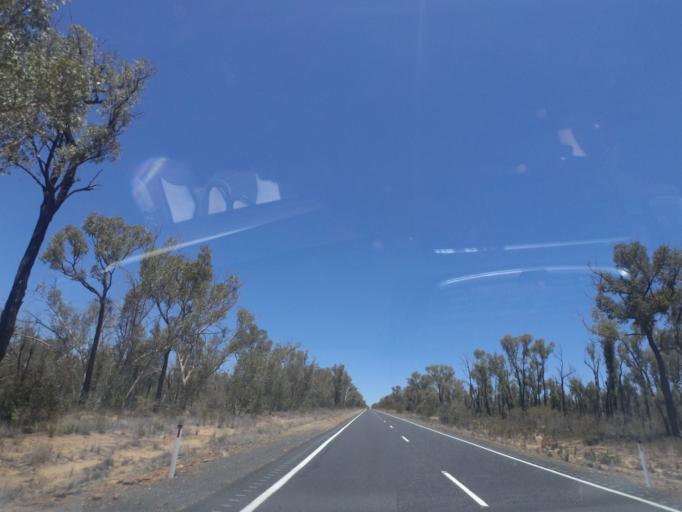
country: AU
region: New South Wales
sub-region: Warrumbungle Shire
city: Coonabarabran
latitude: -30.9477
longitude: 149.4219
